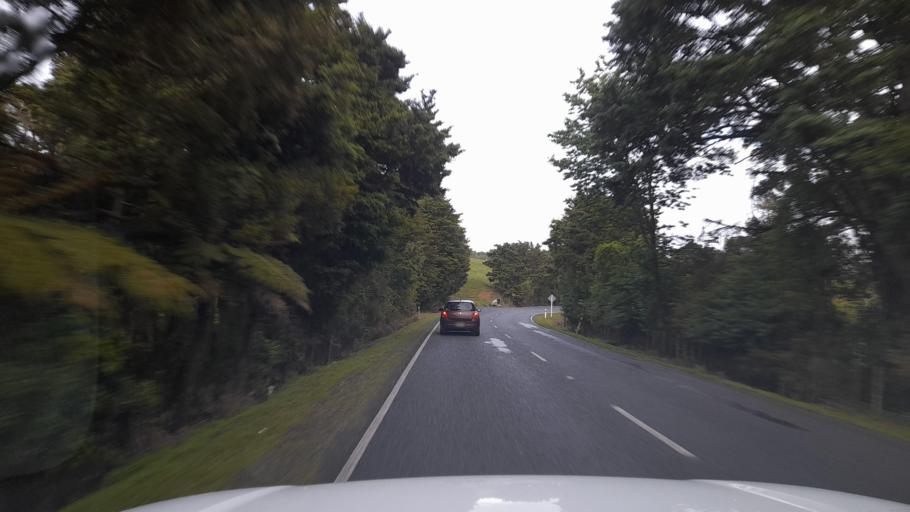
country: NZ
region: Northland
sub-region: Whangarei
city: Maungatapere
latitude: -35.7105
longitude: 174.0034
